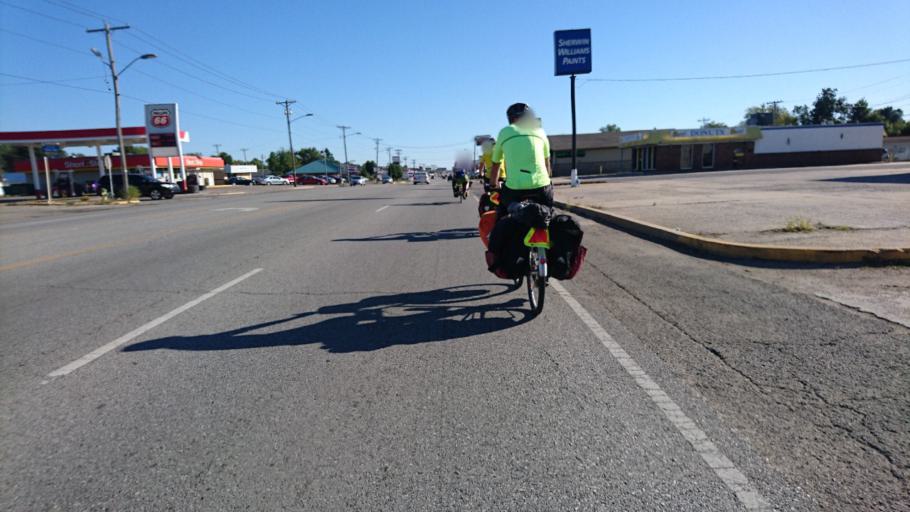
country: US
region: Oklahoma
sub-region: Ottawa County
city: Miami
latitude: 36.8968
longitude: -94.8776
